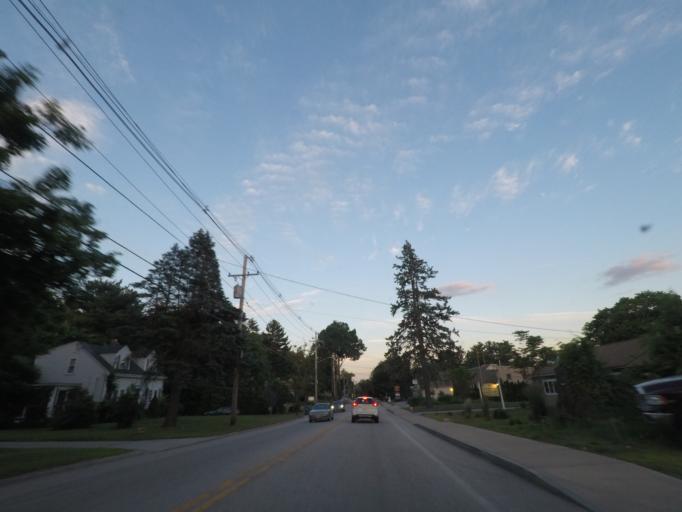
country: US
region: Massachusetts
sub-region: Worcester County
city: Southbridge
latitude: 42.0860
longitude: -72.0580
